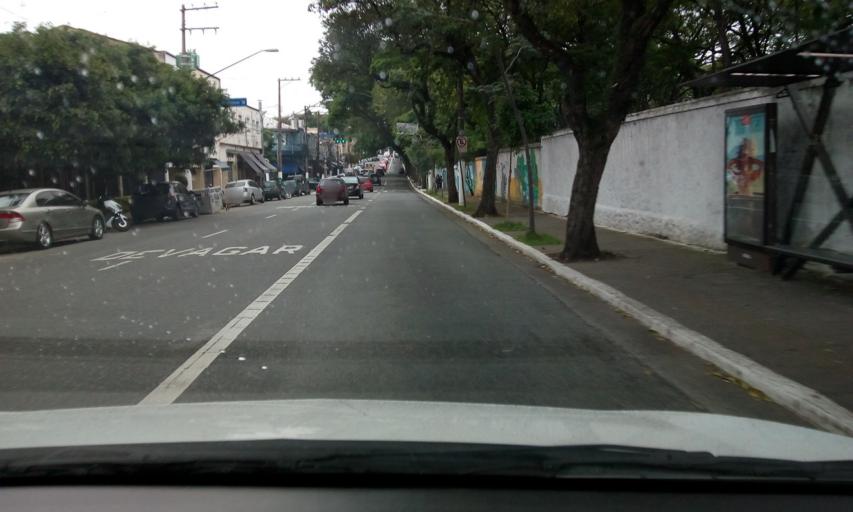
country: BR
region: Sao Paulo
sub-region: Sao Paulo
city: Sao Paulo
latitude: -23.5789
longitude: -46.6257
